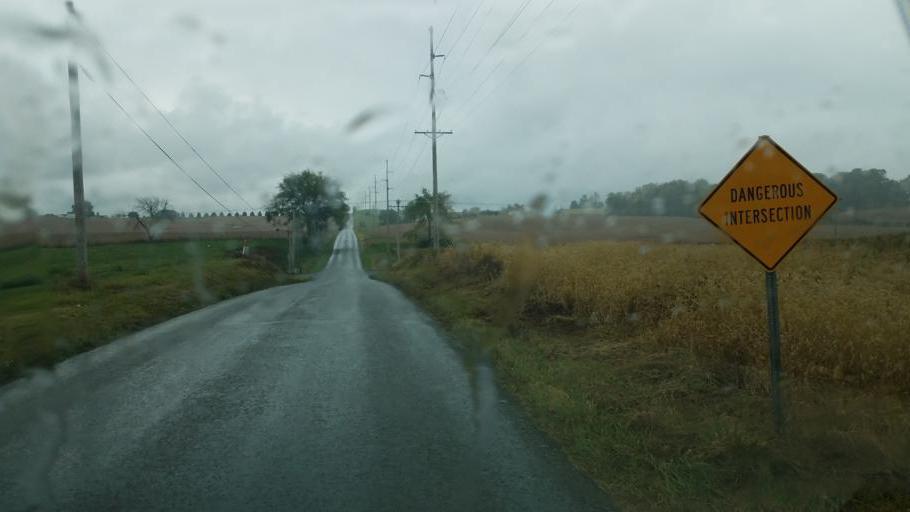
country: US
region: Ohio
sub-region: Holmes County
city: Millersburg
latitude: 40.5849
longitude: -81.8494
